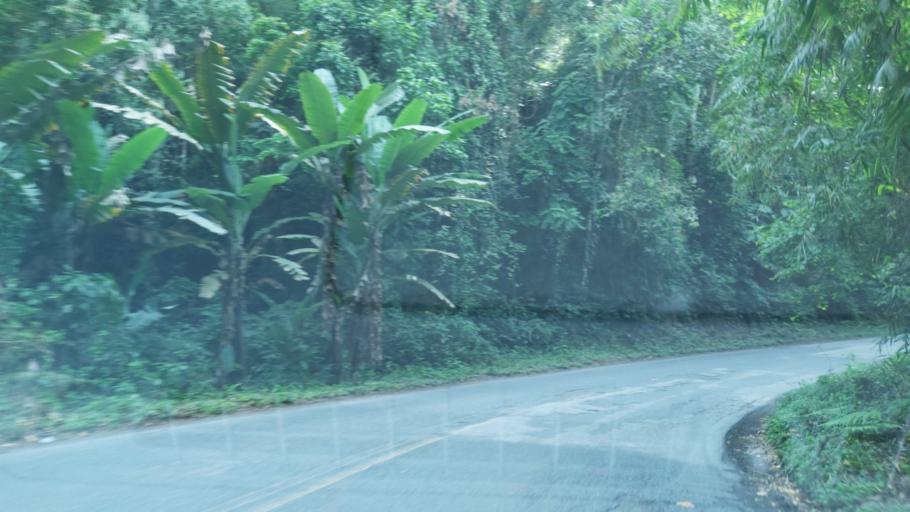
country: BR
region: Sao Paulo
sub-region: Juquia
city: Juquia
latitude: -24.0980
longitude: -47.6201
